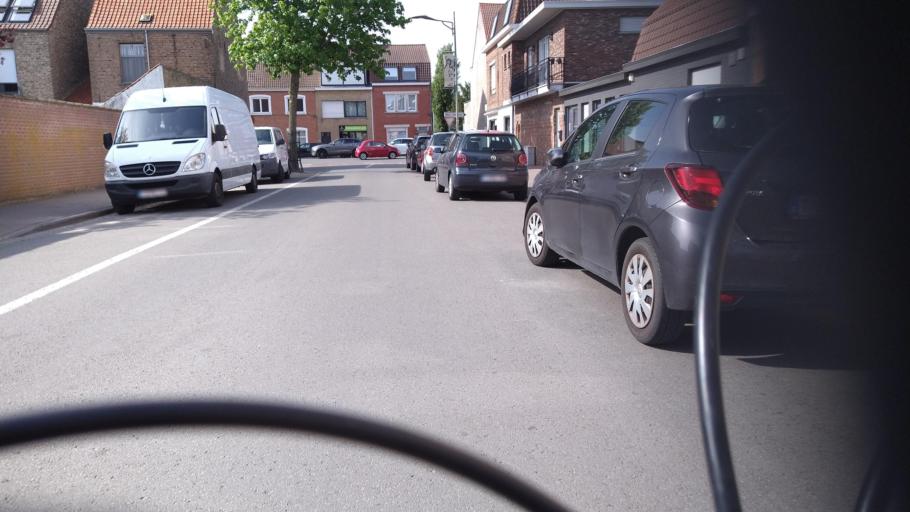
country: BE
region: Flanders
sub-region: Provincie West-Vlaanderen
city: Brugge
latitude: 51.1963
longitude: 3.1784
